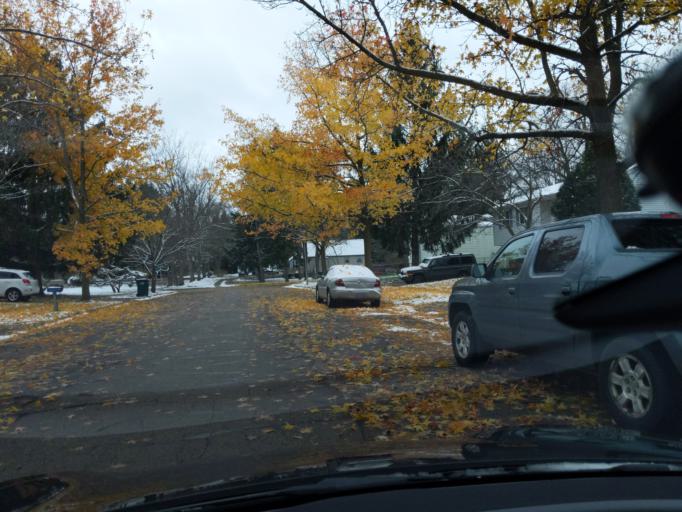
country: US
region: Michigan
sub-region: Eaton County
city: Dimondale
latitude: 42.6797
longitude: -84.5969
